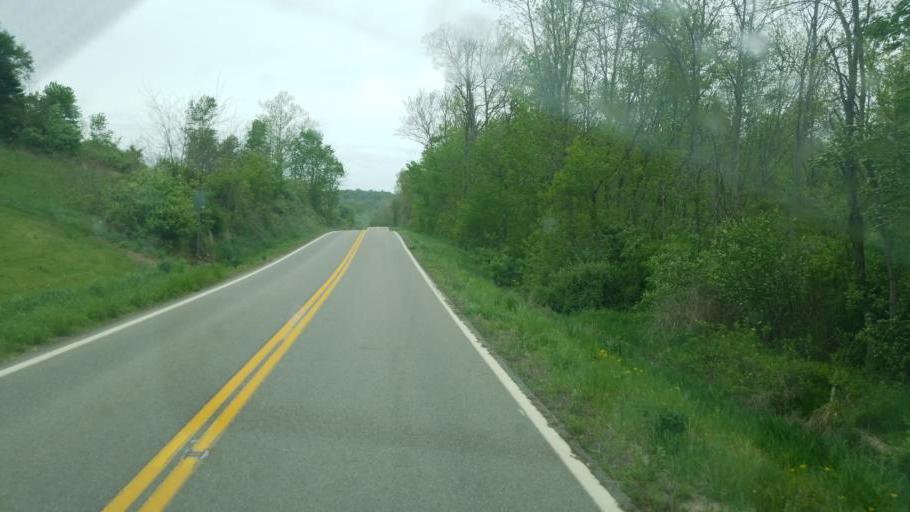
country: US
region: Ohio
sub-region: Guernsey County
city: Mantua
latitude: 40.1590
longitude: -81.6077
